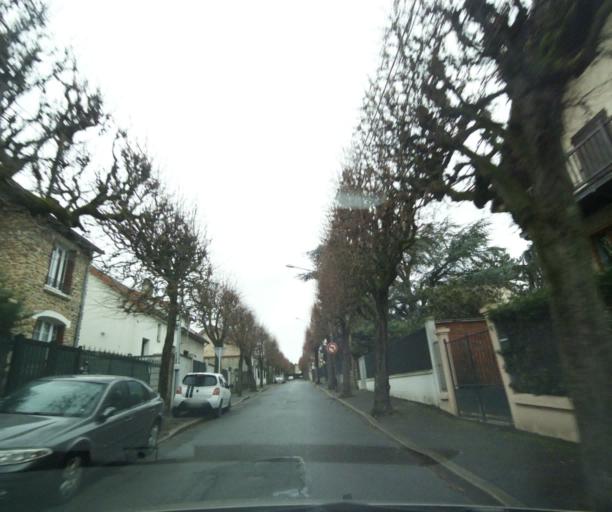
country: FR
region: Ile-de-France
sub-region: Departement du Val-de-Marne
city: Ablon-sur-Seine
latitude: 48.7402
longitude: 2.4185
